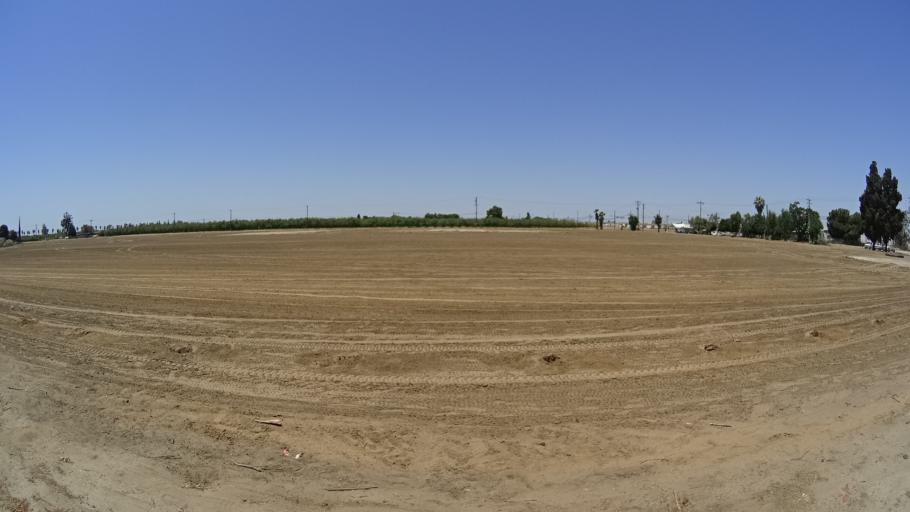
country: US
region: California
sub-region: Fresno County
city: West Park
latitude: 36.7349
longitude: -119.8333
